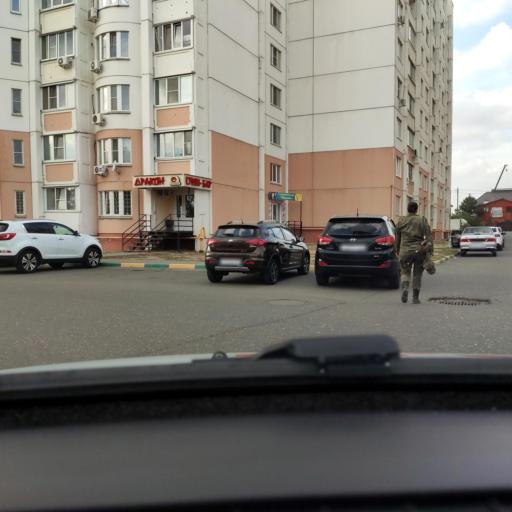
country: RU
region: Voronezj
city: Shilovo
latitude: 51.5626
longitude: 39.1149
